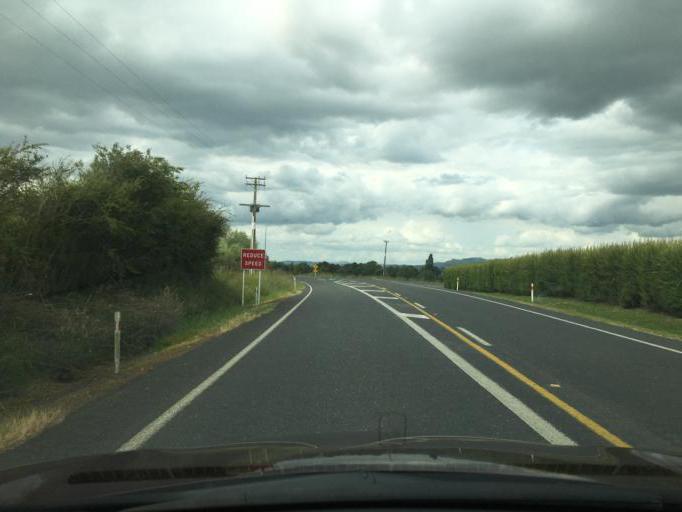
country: NZ
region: Waikato
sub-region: Waipa District
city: Cambridge
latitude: -38.0003
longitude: 175.3932
